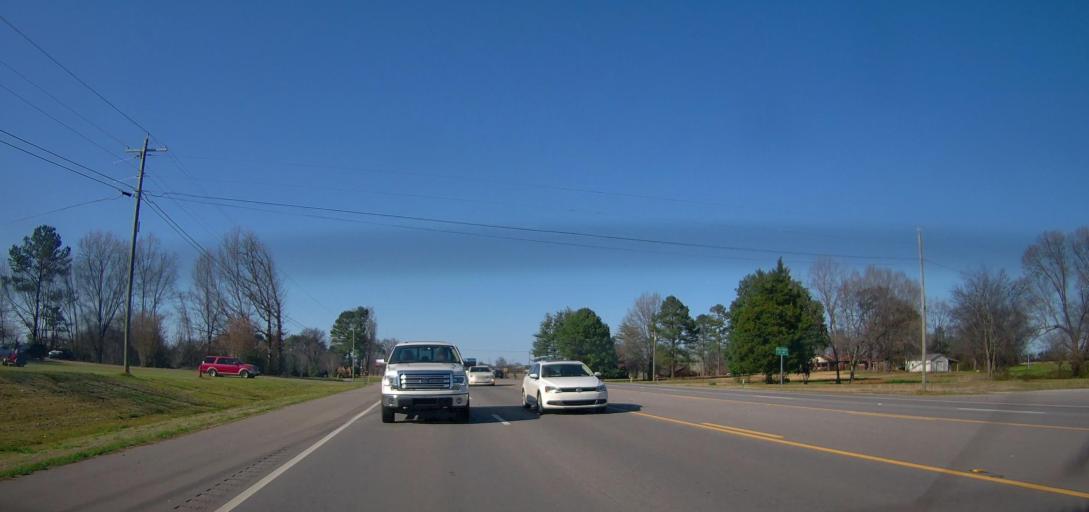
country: US
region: Alabama
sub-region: Colbert County
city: Muscle Shoals
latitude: 34.7073
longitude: -87.6348
